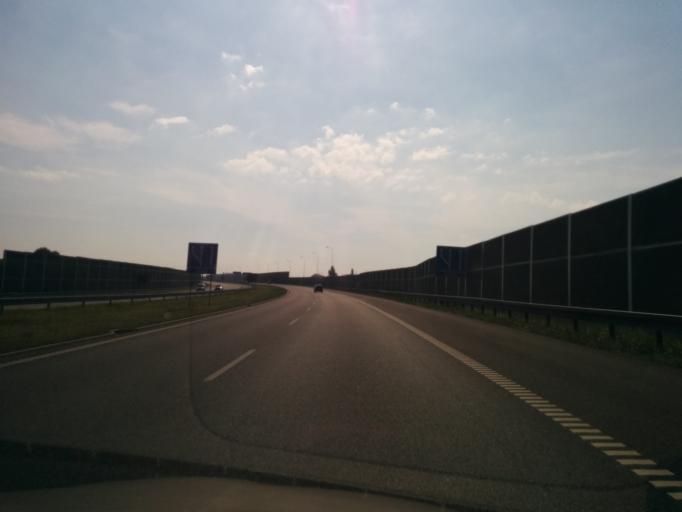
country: PL
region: Silesian Voivodeship
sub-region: Powiat tarnogorski
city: Radzionkow
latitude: 50.3727
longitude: 18.8849
